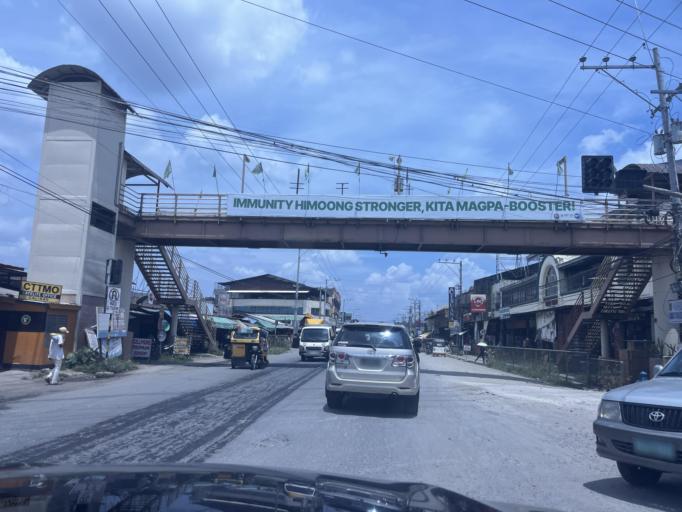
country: PH
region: Davao
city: Lacson
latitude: 7.1908
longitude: 125.4552
